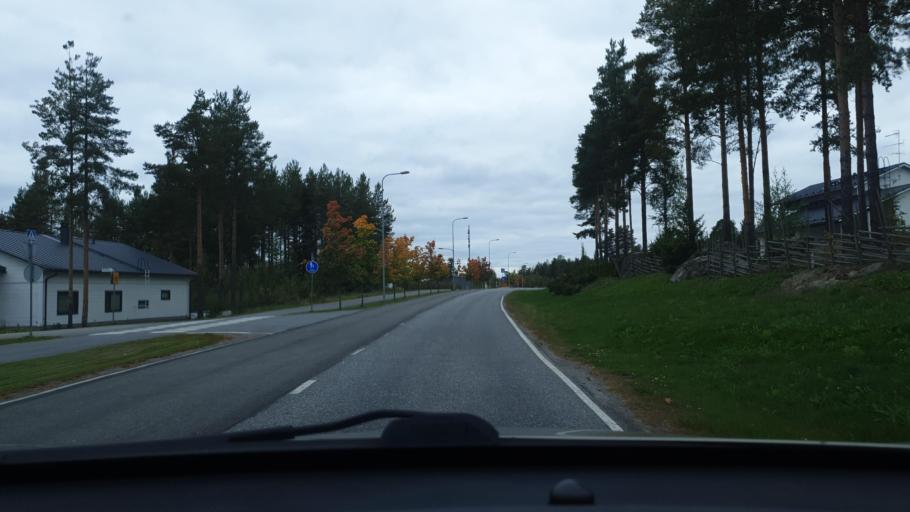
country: FI
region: Ostrobothnia
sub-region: Vaasa
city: Korsholm
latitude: 63.1038
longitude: 21.6767
